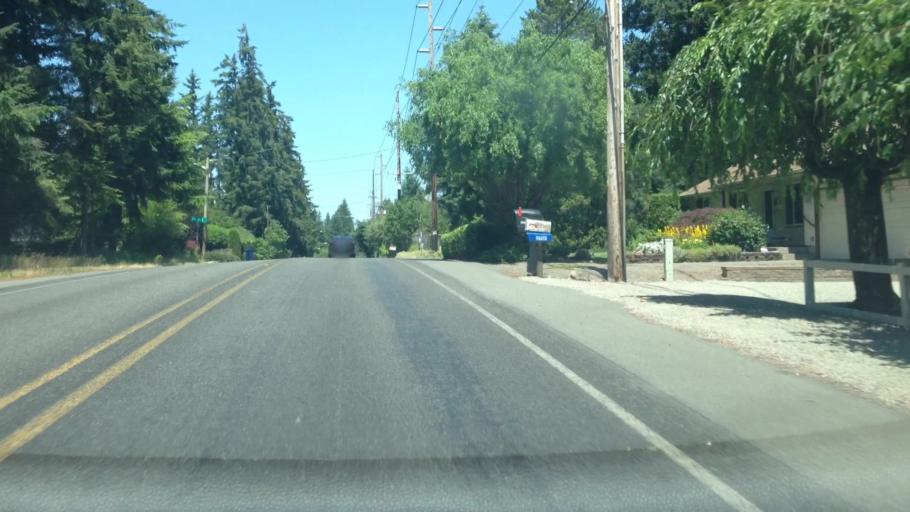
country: US
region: Washington
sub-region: Pierce County
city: Puyallup
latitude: 47.1524
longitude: -122.3148
